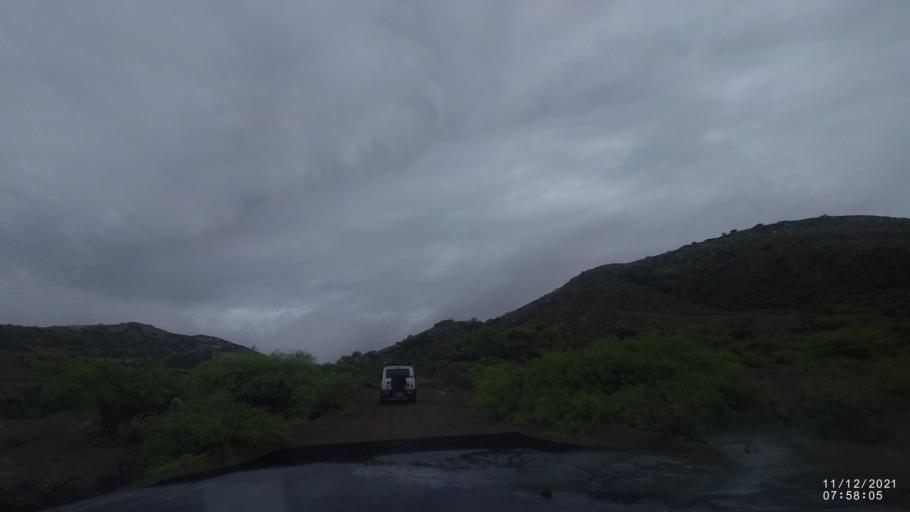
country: BO
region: Cochabamba
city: Tarata
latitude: -17.9463
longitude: -65.9264
